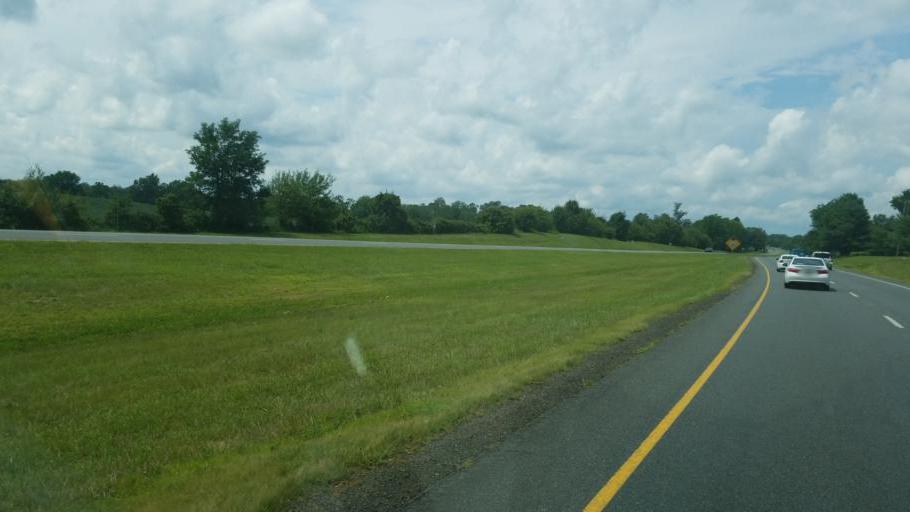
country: US
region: Virginia
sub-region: Fauquier County
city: Marshall
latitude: 38.8513
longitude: -77.8345
